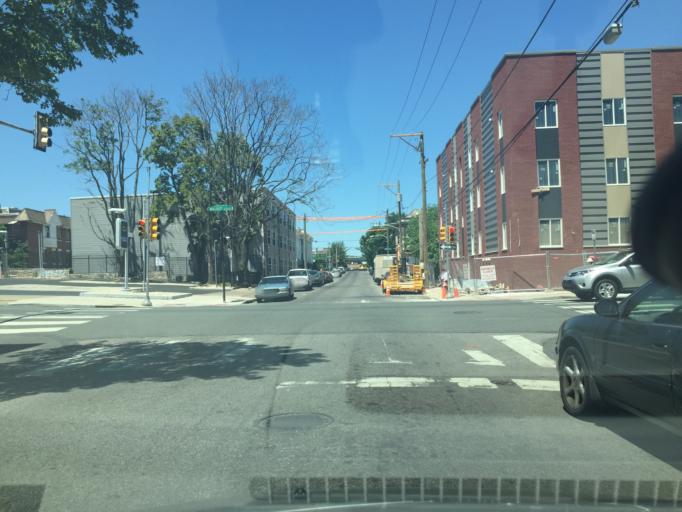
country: US
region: Pennsylvania
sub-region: Delaware County
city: Millbourne
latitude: 39.9553
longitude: -75.2137
